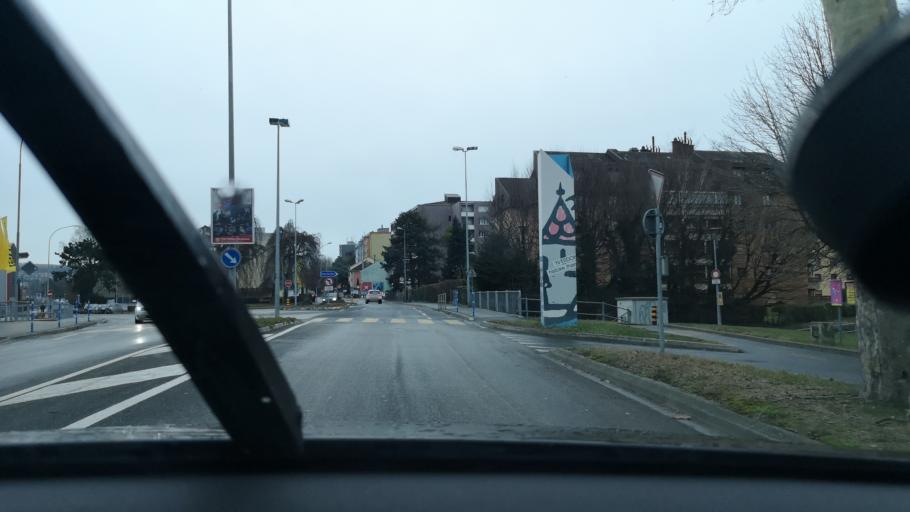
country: CH
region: Vaud
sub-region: Jura-Nord vaudois District
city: Yverdon-les-Bains
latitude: 46.7853
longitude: 6.6326
